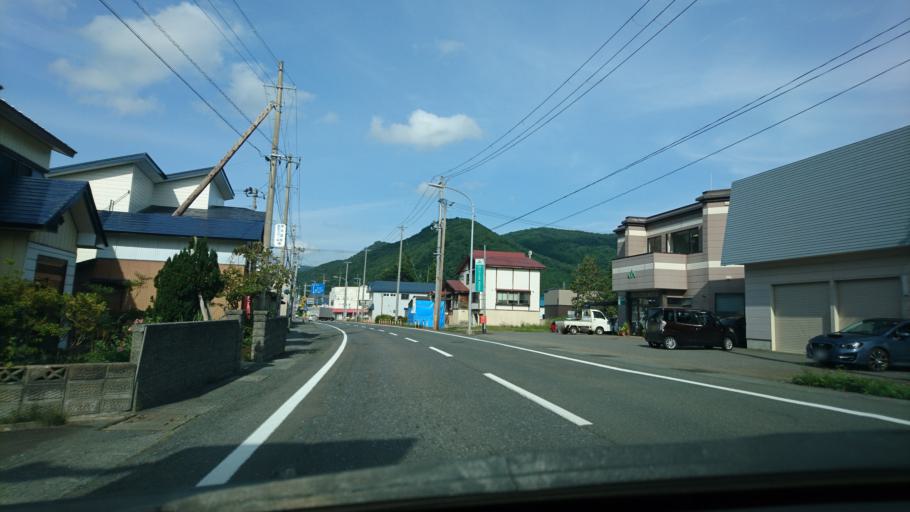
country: JP
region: Akita
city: Yokotemachi
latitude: 39.3159
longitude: 140.7760
